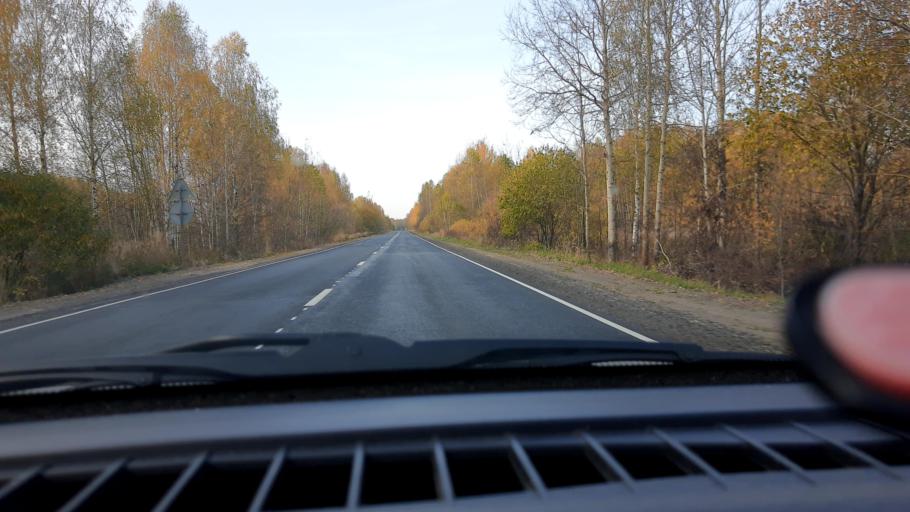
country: RU
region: Nizjnij Novgorod
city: Lukino
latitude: 56.5363
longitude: 43.7845
